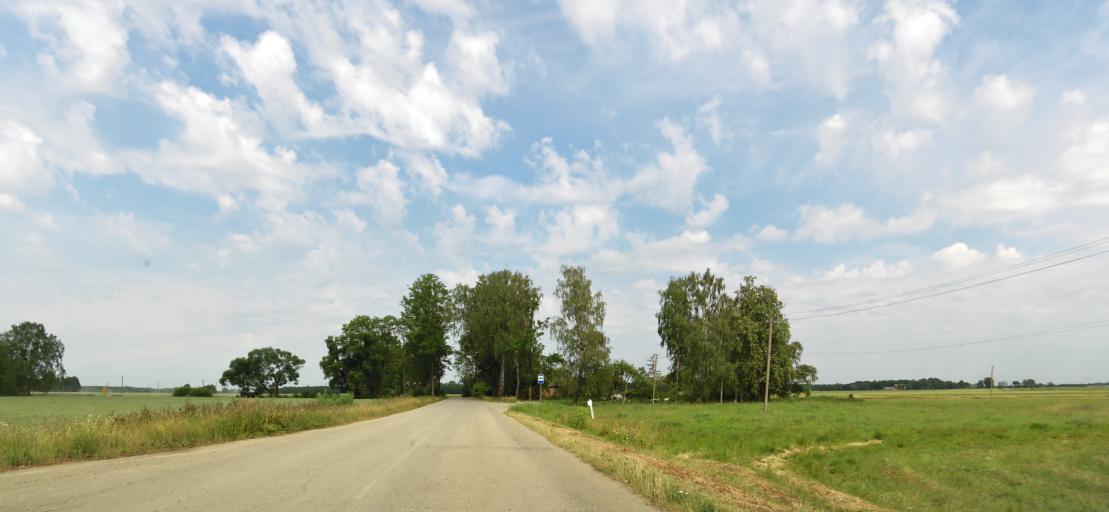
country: LT
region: Panevezys
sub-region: Birzai
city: Birzai
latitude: 56.2742
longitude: 24.6005
